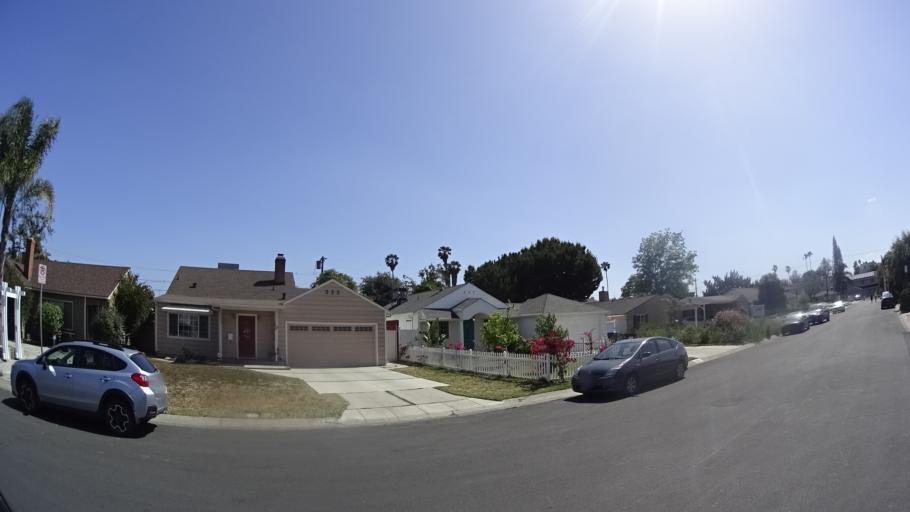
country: US
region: California
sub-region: Los Angeles County
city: North Hollywood
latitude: 34.1755
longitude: -118.3942
